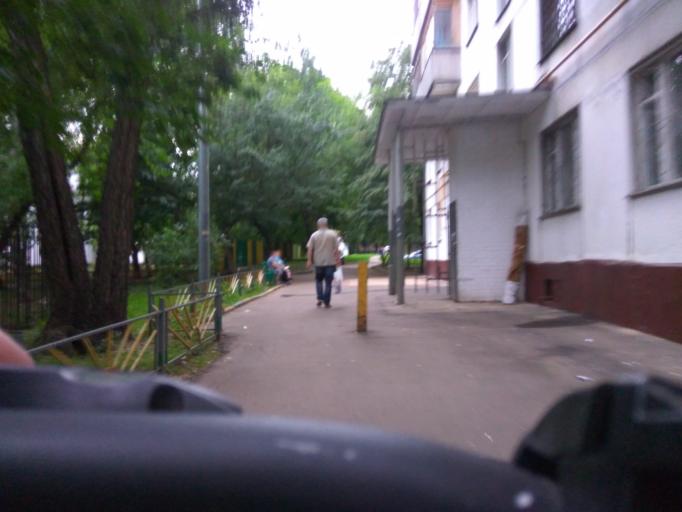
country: RU
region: Moscow
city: Tsaritsyno
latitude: 55.6253
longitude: 37.6543
